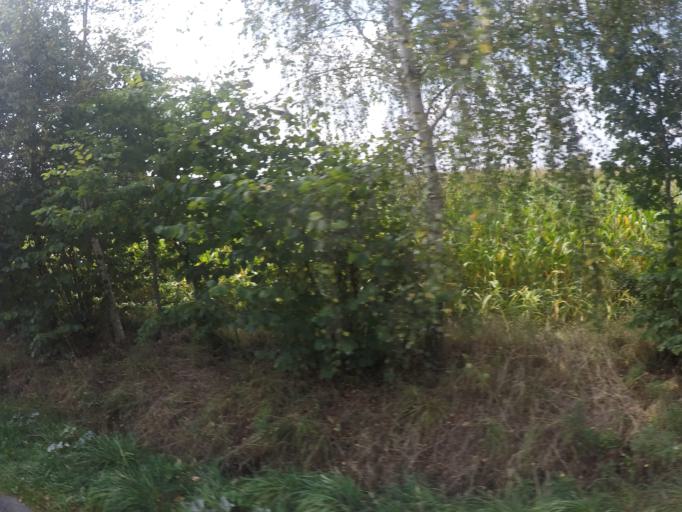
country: FR
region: Brittany
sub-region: Departement des Cotes-d'Armor
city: Lantic
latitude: 48.5554
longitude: -2.8917
